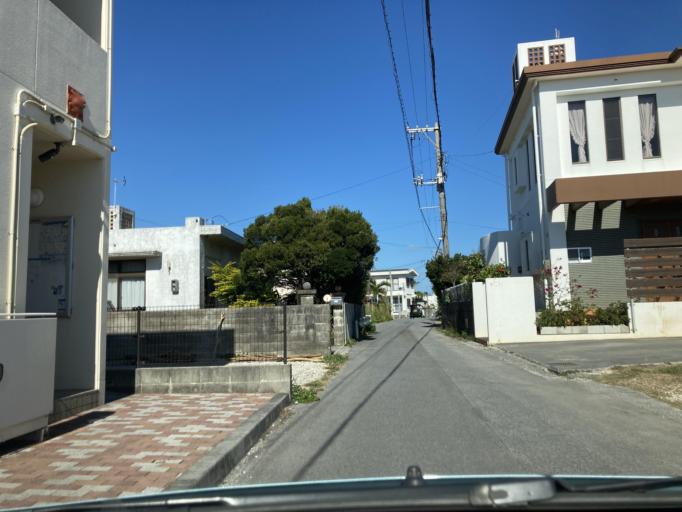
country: JP
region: Okinawa
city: Okinawa
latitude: 26.3643
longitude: 127.8268
